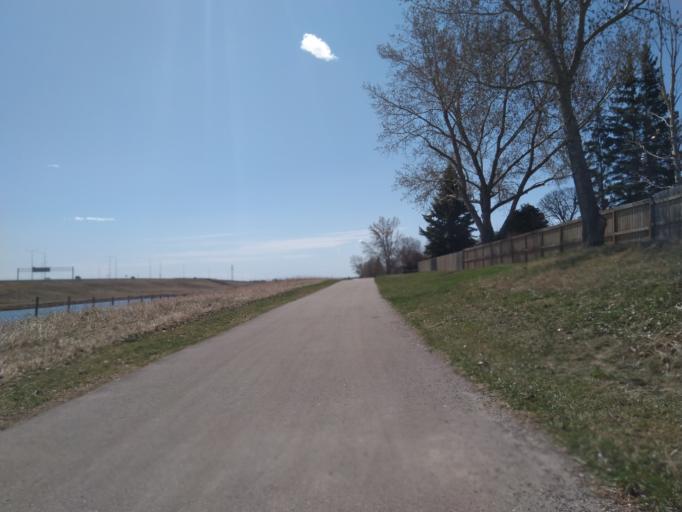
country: CA
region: Alberta
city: Chestermere
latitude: 51.0617
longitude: -113.9234
